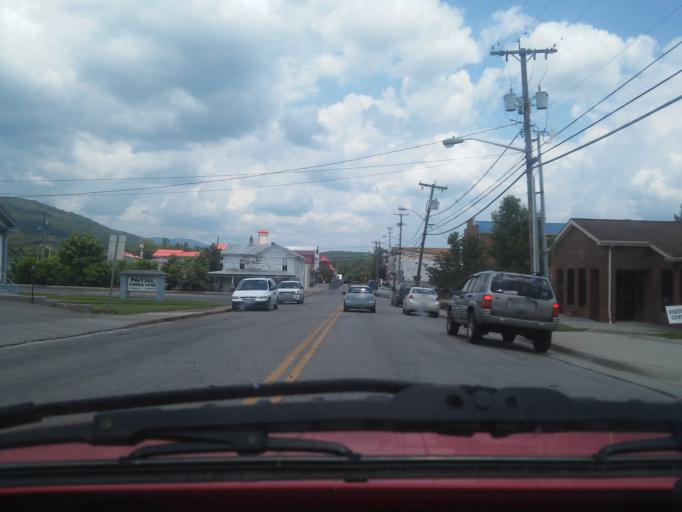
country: US
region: Virginia
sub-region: Craig County
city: New Castle
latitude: 37.5023
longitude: -80.1107
